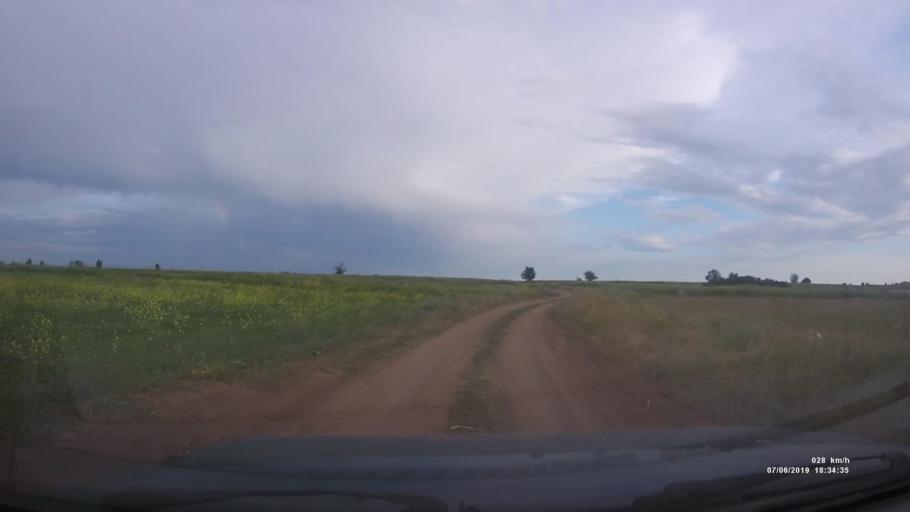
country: RU
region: Rostov
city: Staraya Stanitsa
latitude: 48.2575
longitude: 40.3624
